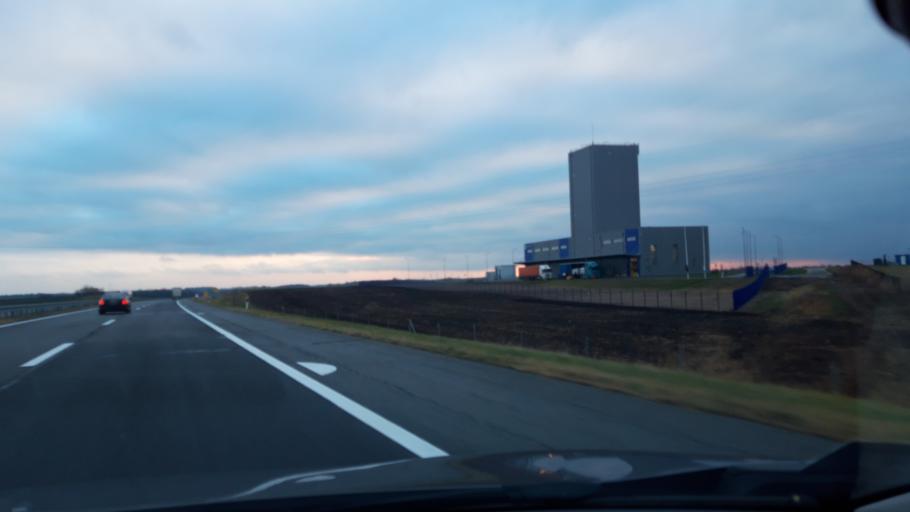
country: RS
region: Autonomna Pokrajina Vojvodina
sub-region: Severnobacki Okrug
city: Mali Igos
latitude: 45.6561
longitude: 19.7237
